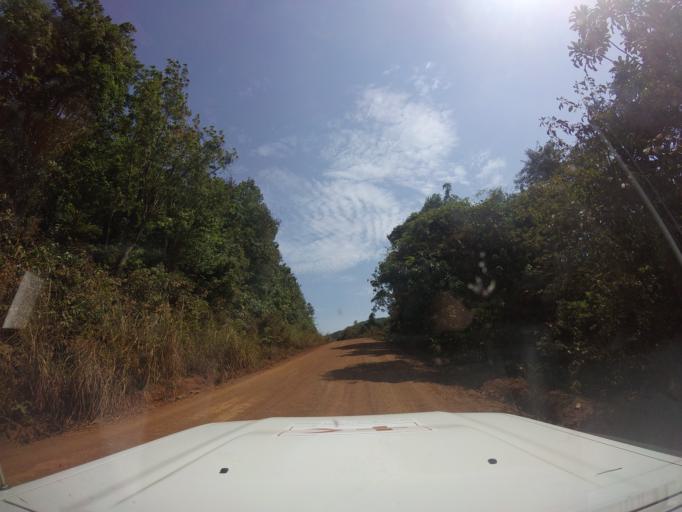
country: LR
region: Grand Cape Mount
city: Robertsport
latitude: 6.7351
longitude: -11.3404
